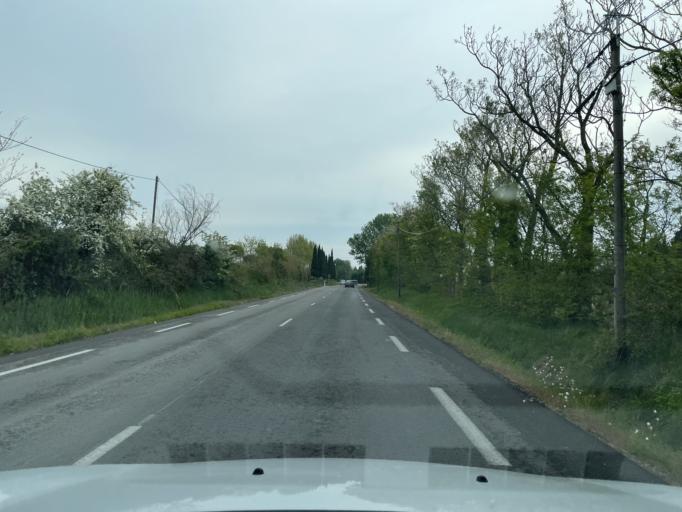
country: FR
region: Provence-Alpes-Cote d'Azur
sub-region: Departement des Bouches-du-Rhone
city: Tarascon
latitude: 43.8159
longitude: 4.6766
